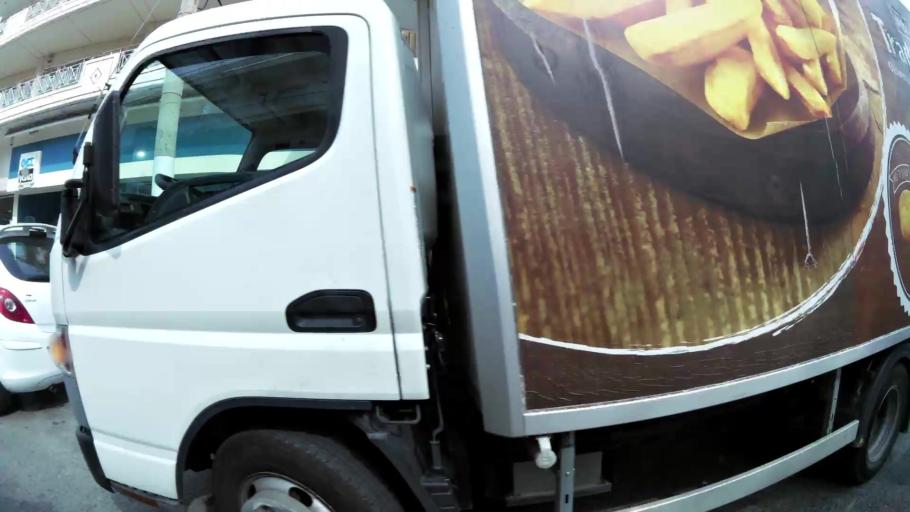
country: GR
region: Attica
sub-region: Nomarchia Athinas
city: Peristeri
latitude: 38.0088
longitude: 23.6811
